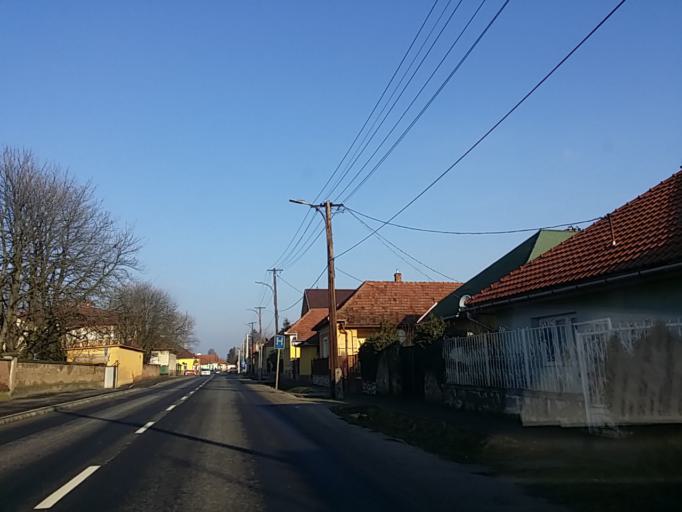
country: HU
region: Borsod-Abauj-Zemplen
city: Mezokovesd
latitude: 47.8051
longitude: 20.5664
